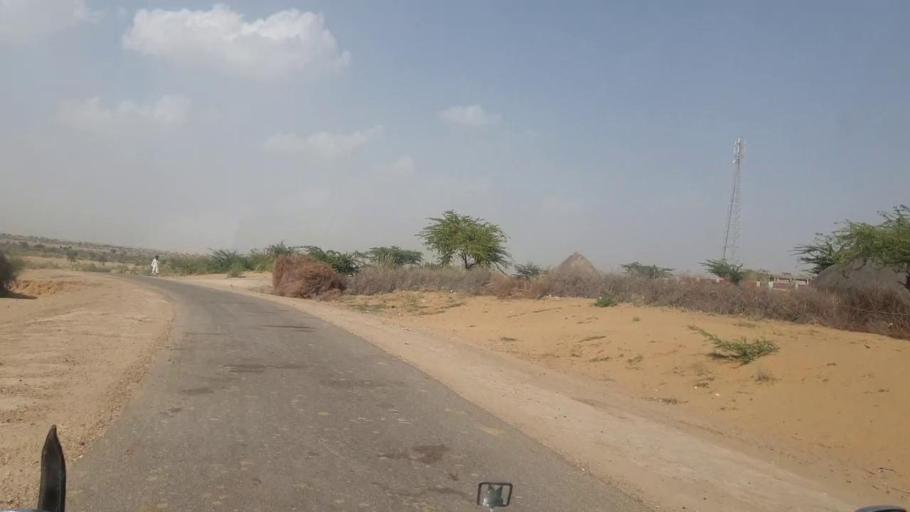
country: PK
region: Sindh
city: Islamkot
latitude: 25.2190
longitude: 70.2889
